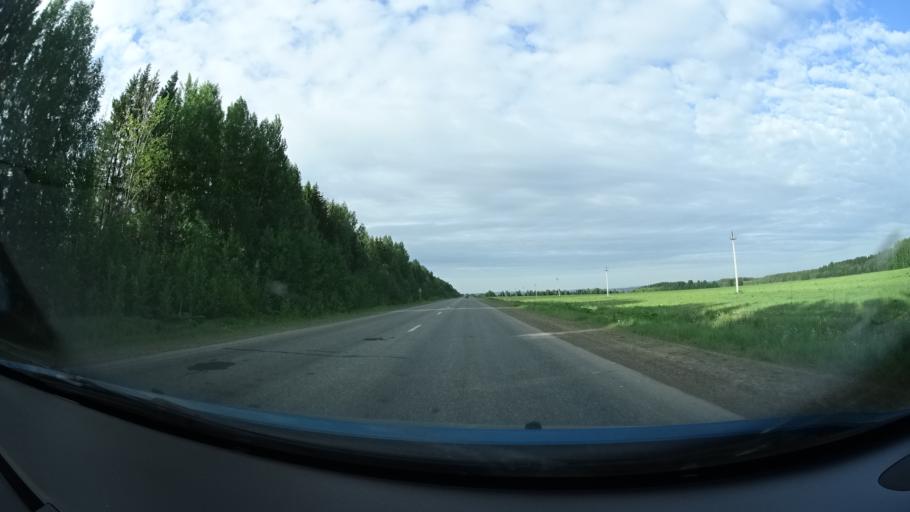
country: RU
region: Perm
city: Osa
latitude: 57.3492
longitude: 55.5943
